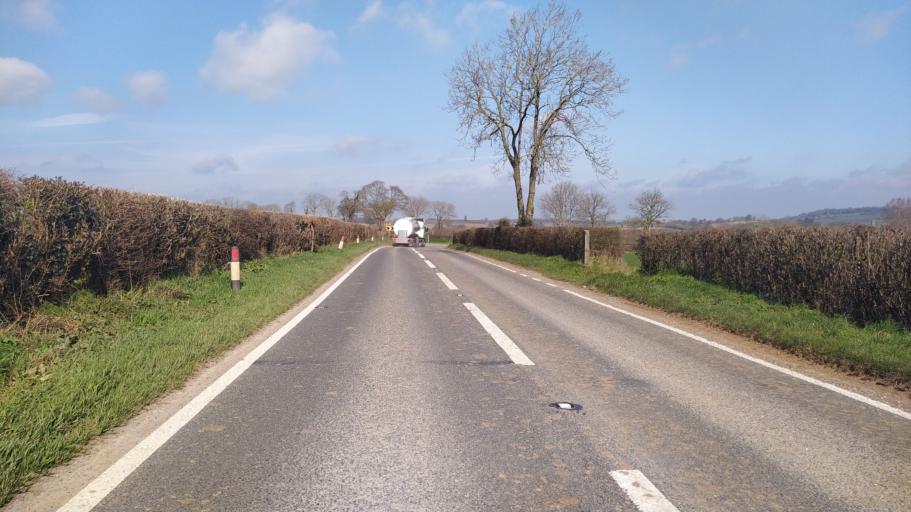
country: GB
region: England
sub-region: Somerset
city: Merriott
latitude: 50.9237
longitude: -2.7731
